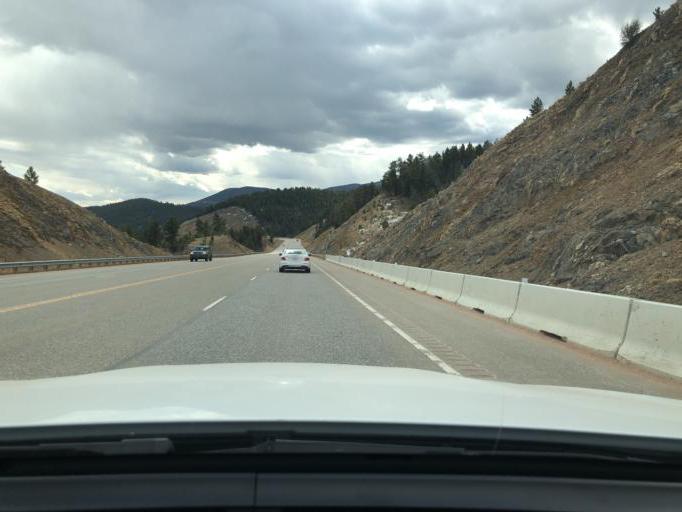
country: US
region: Colorado
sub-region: Gilpin County
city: Central City
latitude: 39.7746
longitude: -105.4734
